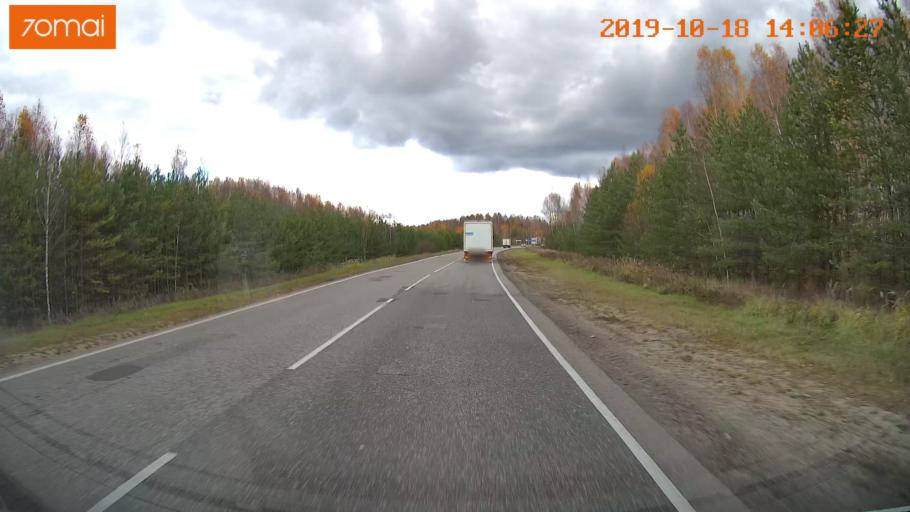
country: RU
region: Rjazan
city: Spas-Klepiki
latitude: 55.1454
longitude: 40.1502
